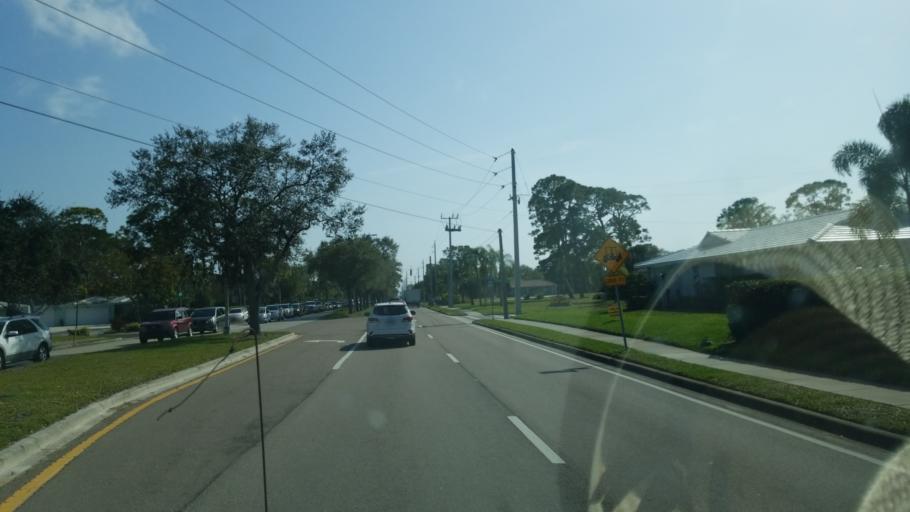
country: US
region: Florida
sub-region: Sarasota County
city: Southgate
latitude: 27.3203
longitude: -82.4965
